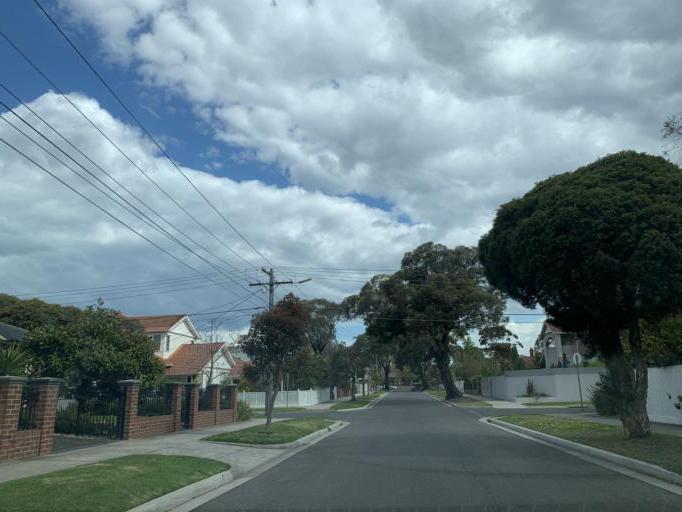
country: AU
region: Victoria
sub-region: Bayside
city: Hampton
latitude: -37.9349
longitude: 145.0132
